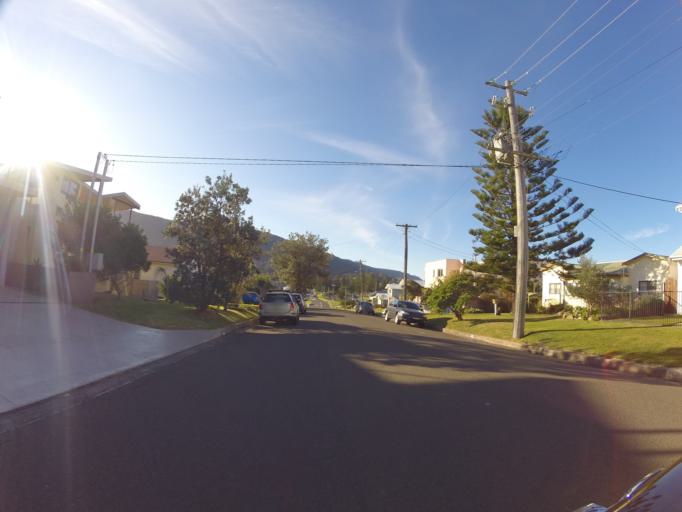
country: AU
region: New South Wales
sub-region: Wollongong
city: Bulli
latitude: -34.3200
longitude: 150.9256
